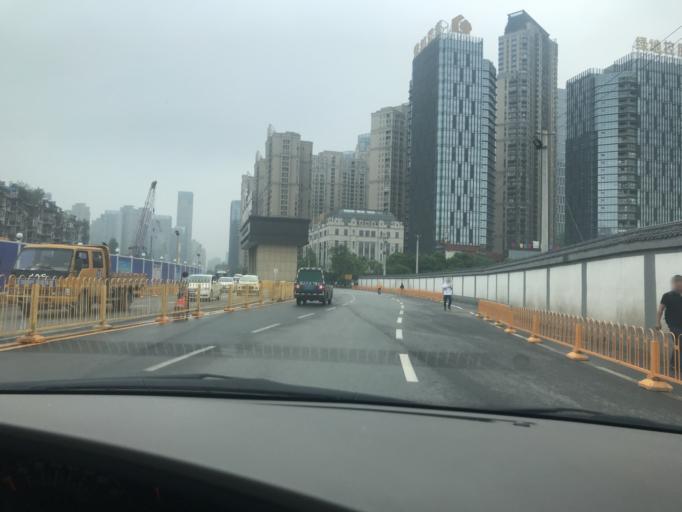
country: CN
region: Hubei
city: Jiang'an
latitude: 30.5861
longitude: 114.3218
